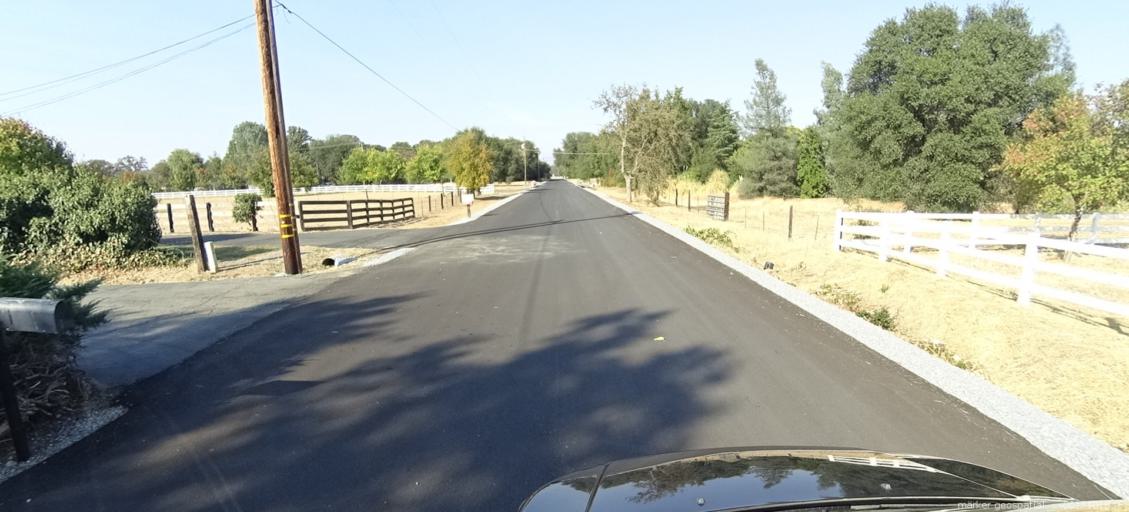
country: US
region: California
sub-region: Shasta County
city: Palo Cedro
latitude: 40.5682
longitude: -122.2458
